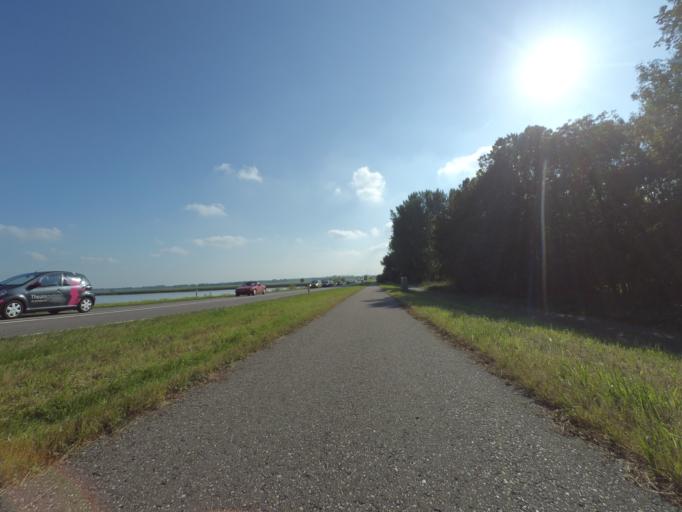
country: NL
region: Gelderland
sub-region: Gemeente Nijkerk
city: Nijkerk
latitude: 52.2602
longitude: 5.4719
